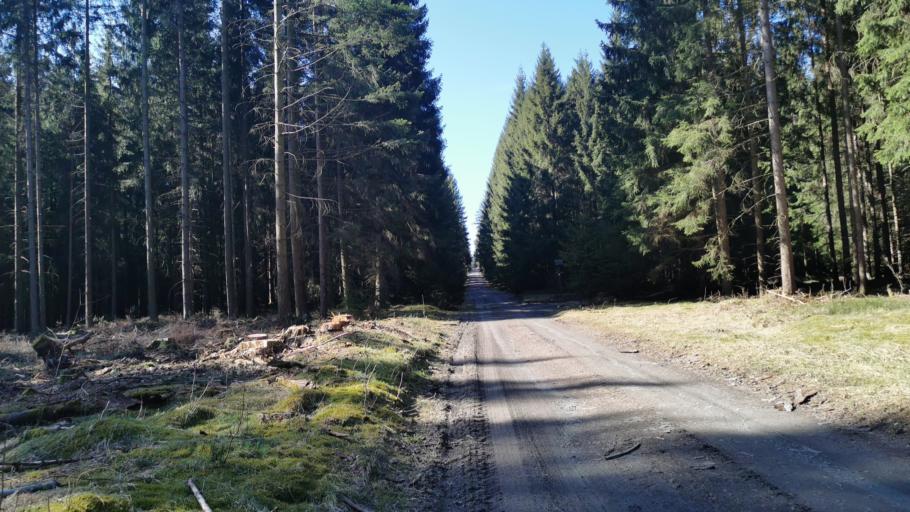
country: DE
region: Thuringia
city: Wurzbach
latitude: 50.4436
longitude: 11.5058
